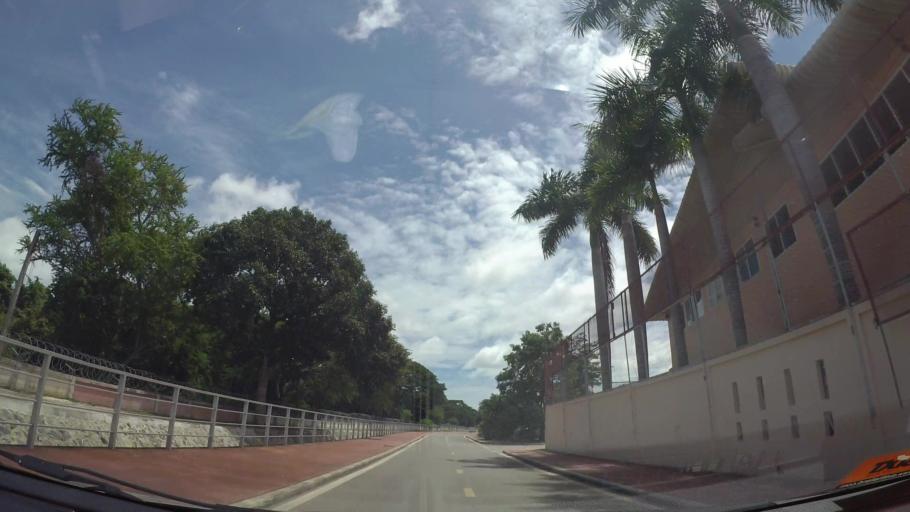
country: TH
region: Chon Buri
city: Sattahip
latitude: 12.7094
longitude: 100.8861
